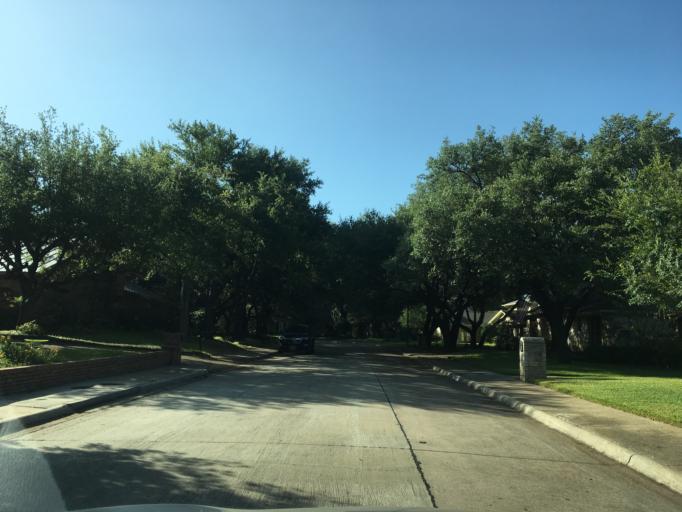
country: US
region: Texas
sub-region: Dallas County
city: Richardson
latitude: 32.8913
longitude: -96.7252
